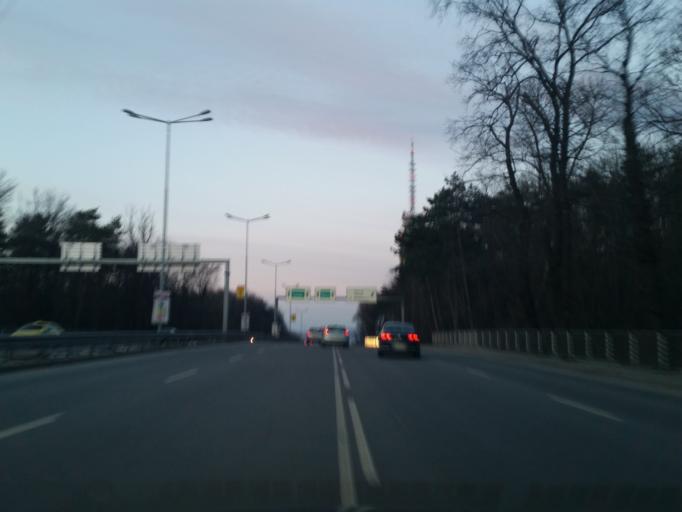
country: BG
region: Sofia-Capital
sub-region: Stolichna Obshtina
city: Sofia
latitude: 42.6745
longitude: 23.3385
